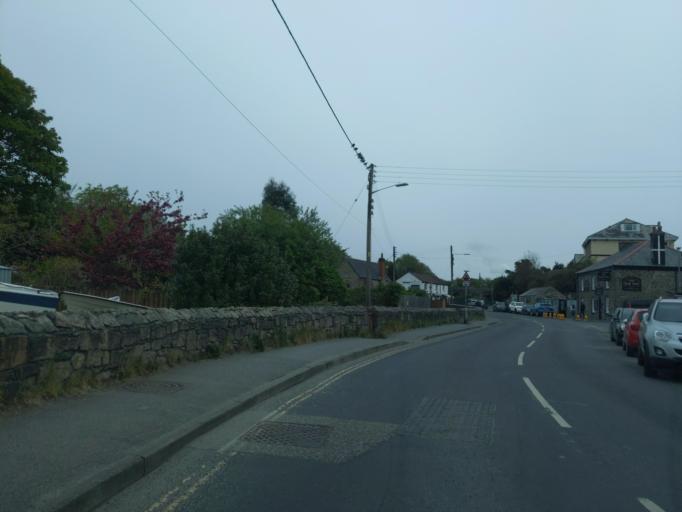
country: GB
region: England
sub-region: Cornwall
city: Par
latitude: 50.3505
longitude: -4.7086
